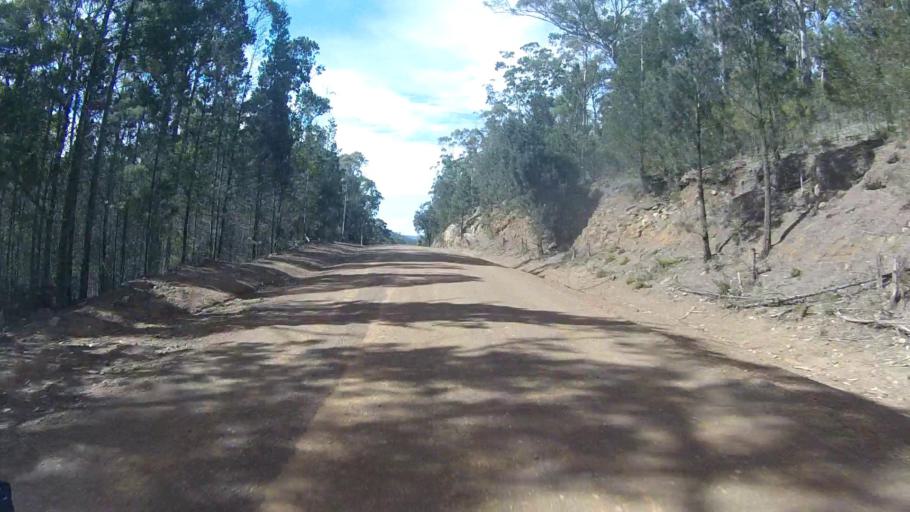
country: AU
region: Tasmania
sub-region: Sorell
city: Sorell
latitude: -42.6132
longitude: 147.8981
